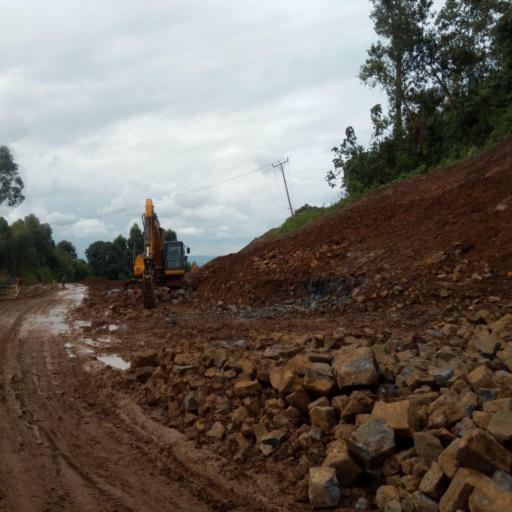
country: ET
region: Oromiya
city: Gore
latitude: 7.7375
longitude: 35.4812
